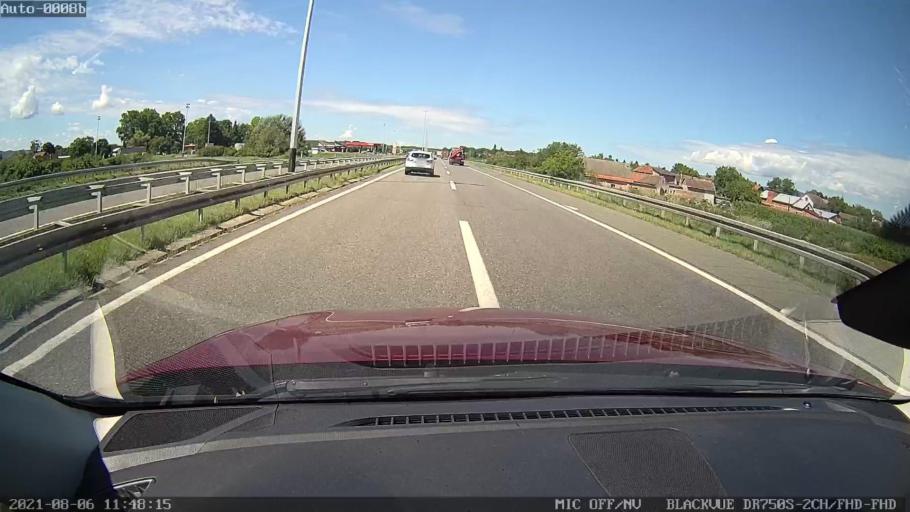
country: HR
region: Brodsko-Posavska
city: Luzani
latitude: 45.1627
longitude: 17.7053
